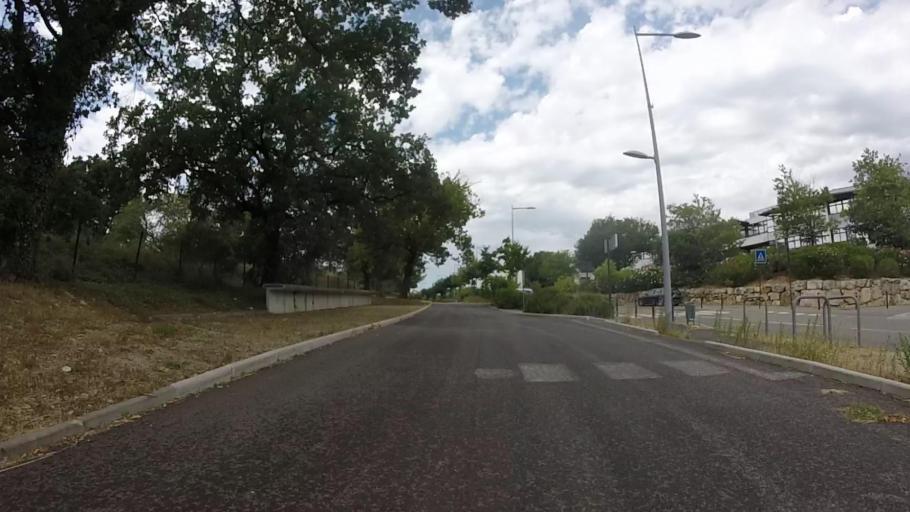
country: FR
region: Provence-Alpes-Cote d'Azur
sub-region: Departement des Alpes-Maritimes
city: Biot
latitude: 43.6229
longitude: 7.0714
